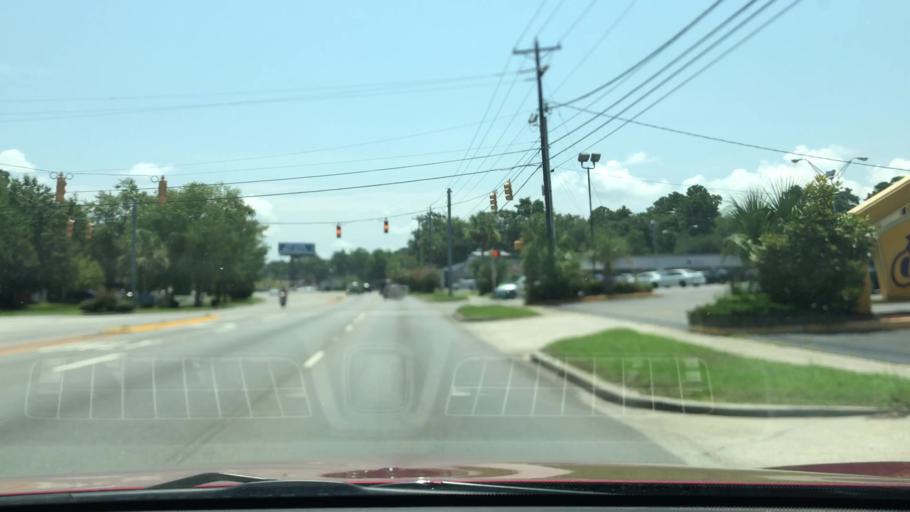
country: US
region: South Carolina
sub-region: Berkeley County
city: Hanahan
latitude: 32.8580
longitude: -80.0444
